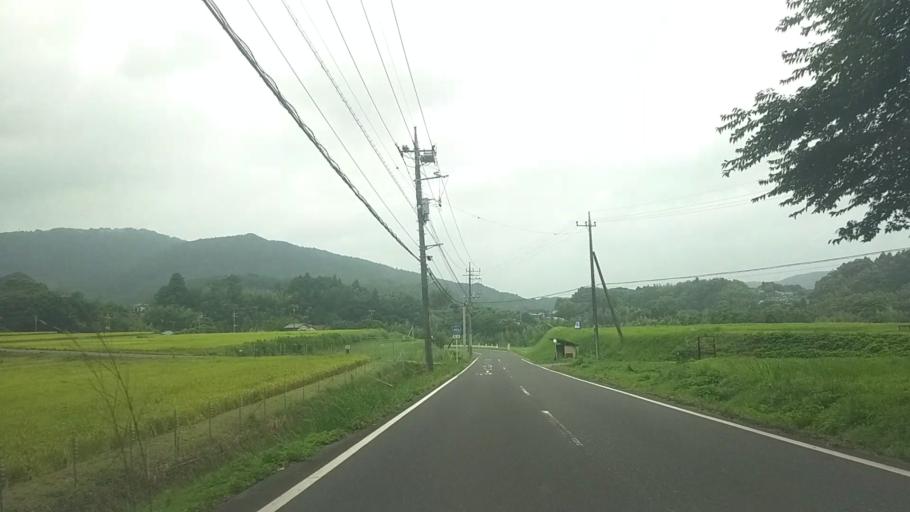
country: JP
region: Chiba
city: Kimitsu
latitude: 35.2425
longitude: 139.9960
